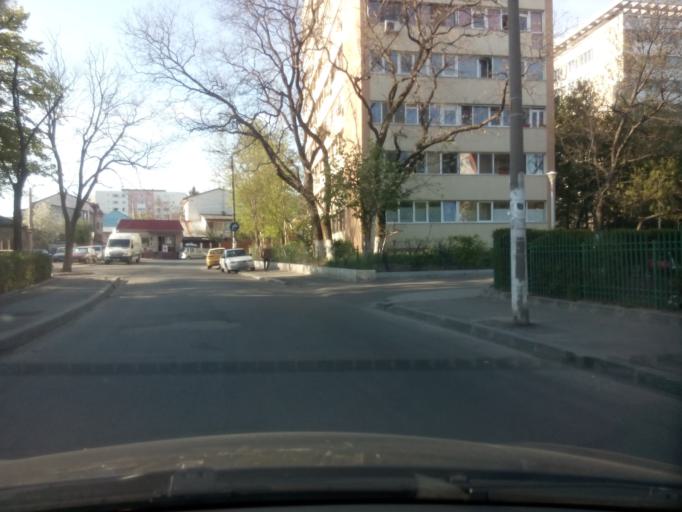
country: RO
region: Ilfov
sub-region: Comuna Fundeni-Dobroesti
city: Fundeni
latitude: 44.4299
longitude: 26.1575
